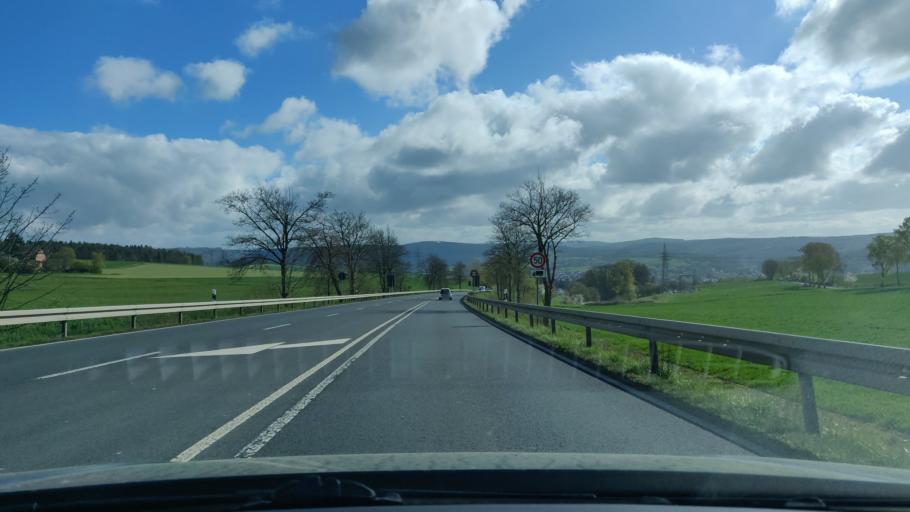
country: DE
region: Hesse
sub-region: Regierungsbezirk Kassel
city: Korle
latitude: 51.1287
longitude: 9.5052
